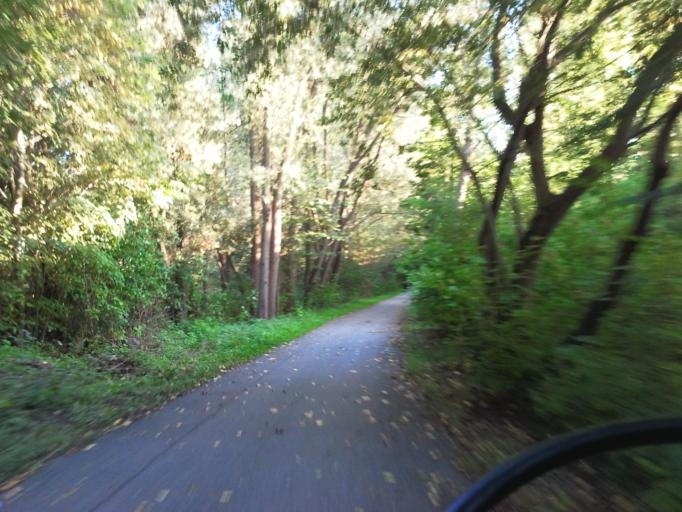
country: DE
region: Mecklenburg-Vorpommern
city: Lambrechtshagen
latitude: 54.1005
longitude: 12.0652
